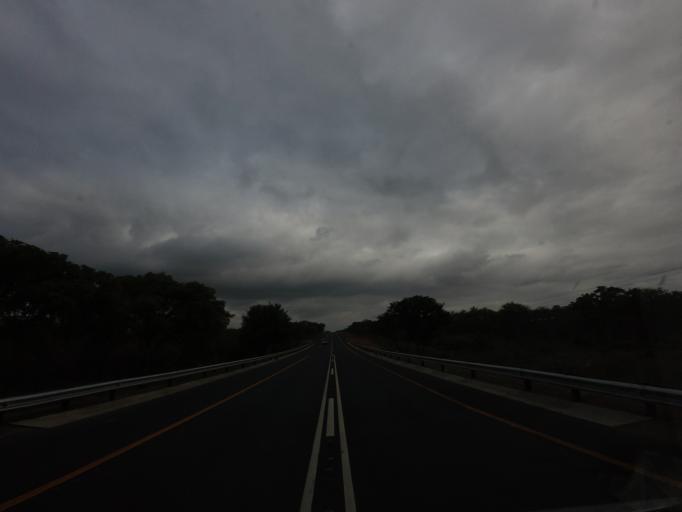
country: ZA
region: Mpumalanga
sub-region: Ehlanzeni District
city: Komatipoort
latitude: -25.4408
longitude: 31.7352
